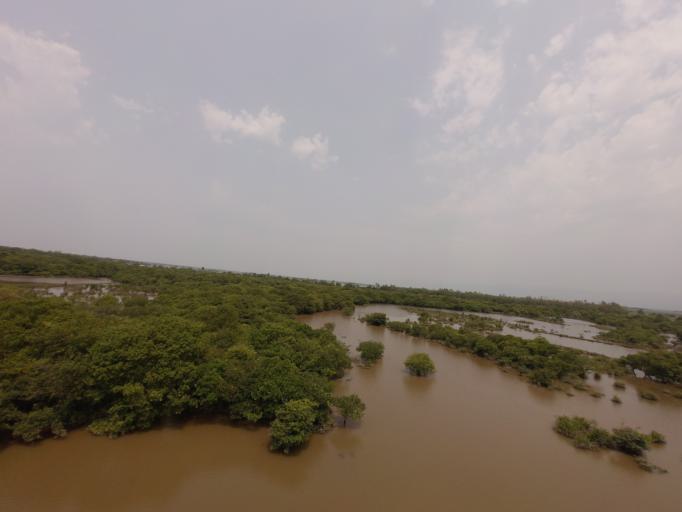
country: BD
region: Sylhet
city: Sylhet
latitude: 25.0131
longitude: 91.9231
